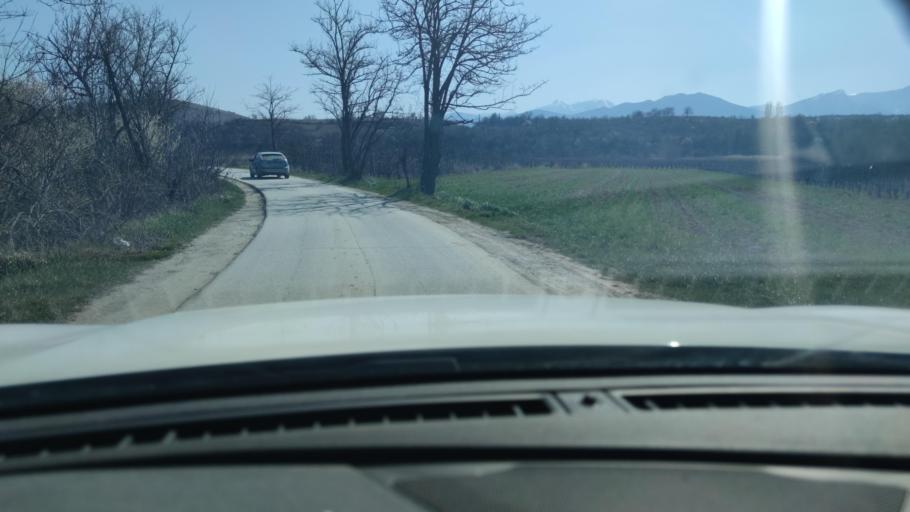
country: MK
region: Rosoman
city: Rosoman
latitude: 41.4746
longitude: 21.9102
